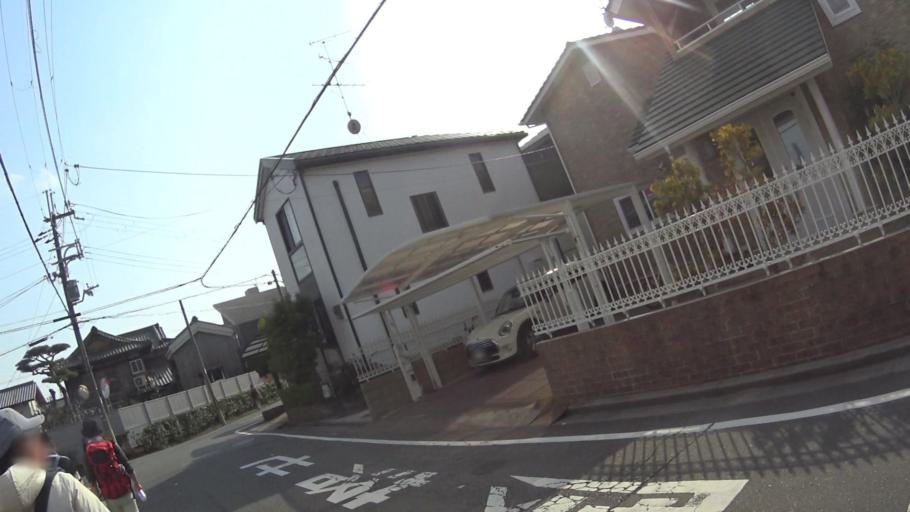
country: JP
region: Nara
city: Nara-shi
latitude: 34.6905
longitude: 135.8226
